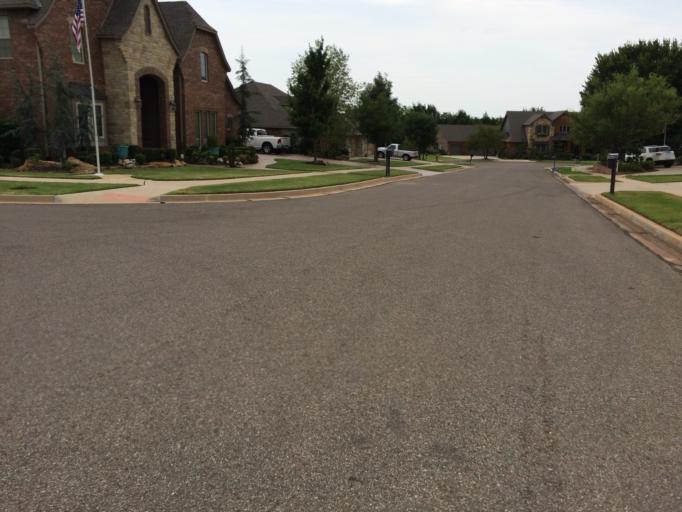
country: US
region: Oklahoma
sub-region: Cleveland County
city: Hall Park
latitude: 35.2407
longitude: -97.4108
